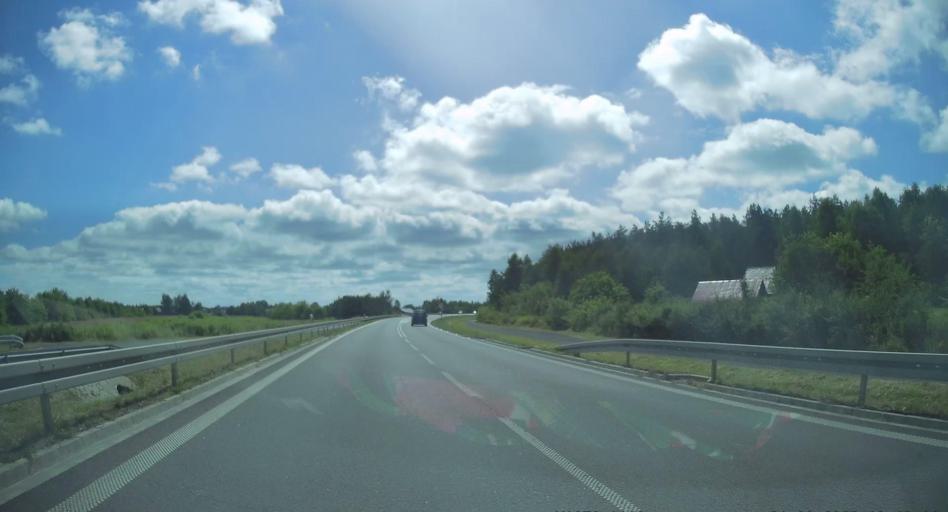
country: PL
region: Subcarpathian Voivodeship
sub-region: Powiat mielecki
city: Padew Narodowa
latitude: 50.3544
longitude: 21.4913
